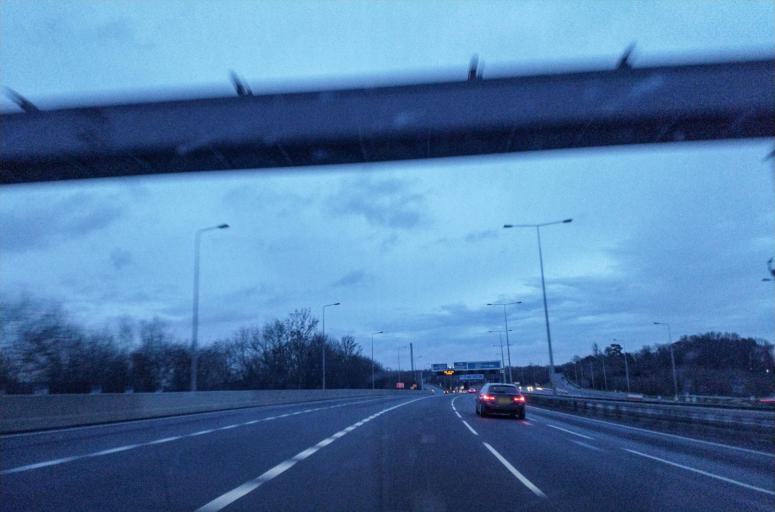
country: GB
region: England
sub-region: Kent
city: Aylesford
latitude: 51.2991
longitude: 0.4769
